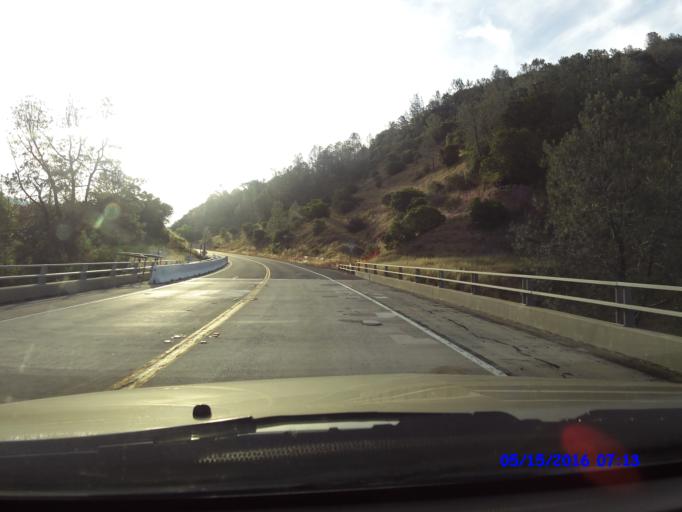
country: US
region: California
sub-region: Tuolumne County
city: Jamestown
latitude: 37.8390
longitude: -120.3767
